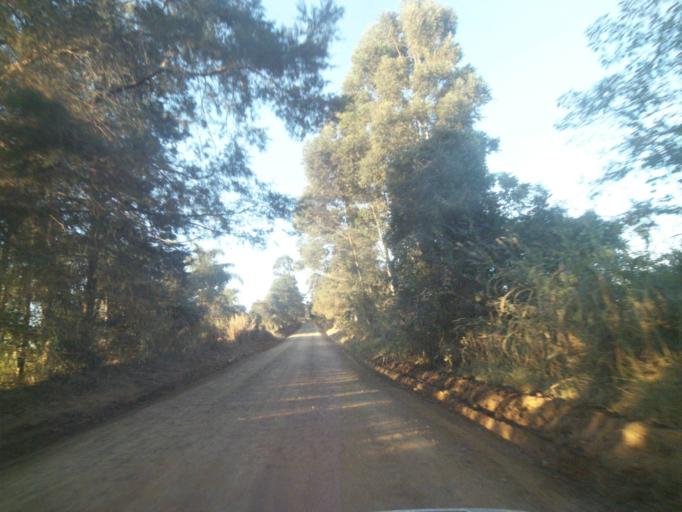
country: BR
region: Parana
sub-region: Tibagi
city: Tibagi
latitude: -24.5304
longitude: -50.5143
